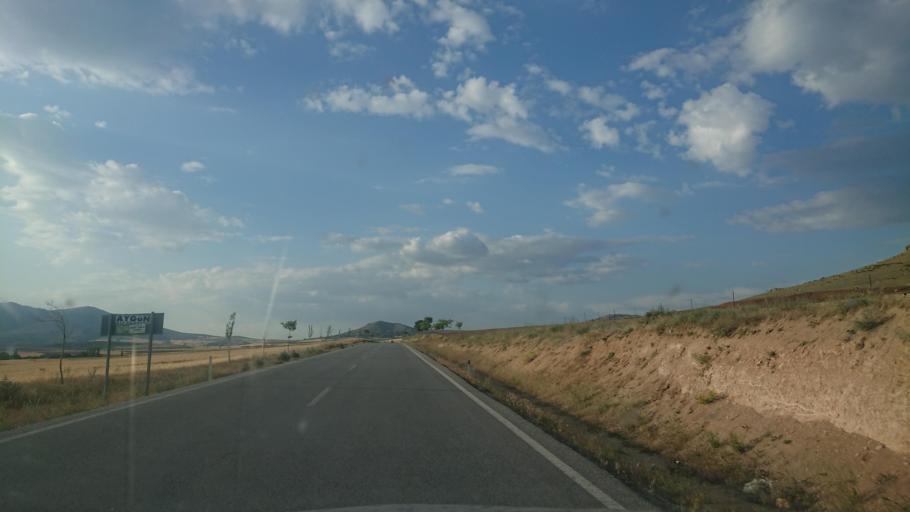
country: TR
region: Aksaray
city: Balci
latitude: 38.5501
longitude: 34.1031
